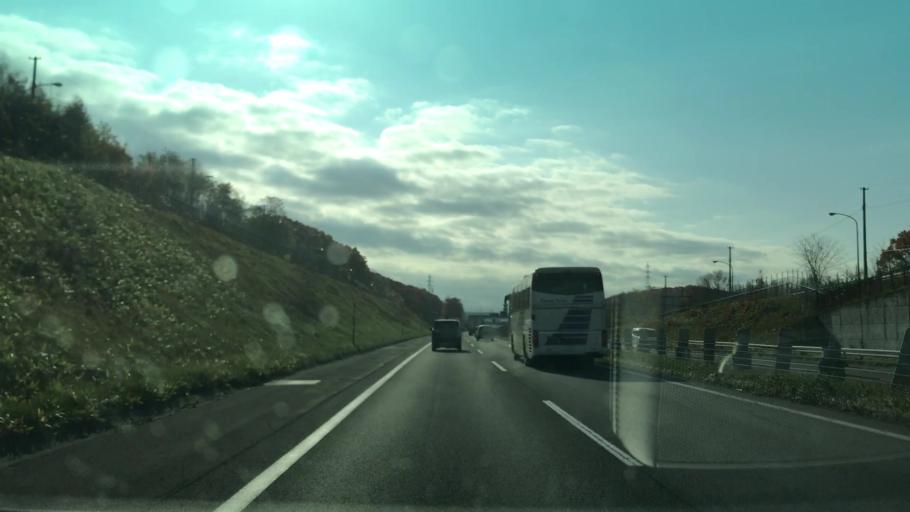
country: JP
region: Hokkaido
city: Kitahiroshima
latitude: 43.0090
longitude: 141.4664
